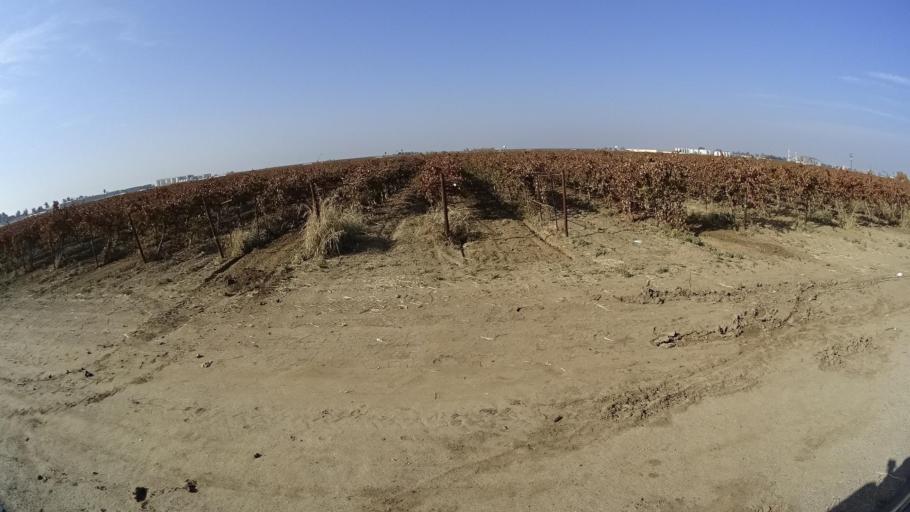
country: US
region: California
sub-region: Kern County
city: McFarland
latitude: 35.7092
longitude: -119.2231
